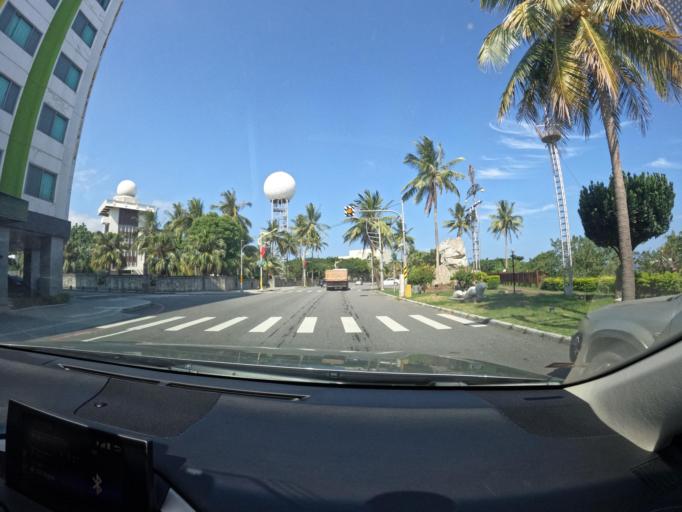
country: TW
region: Taiwan
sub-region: Hualien
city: Hualian
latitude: 23.9877
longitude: 121.6284
